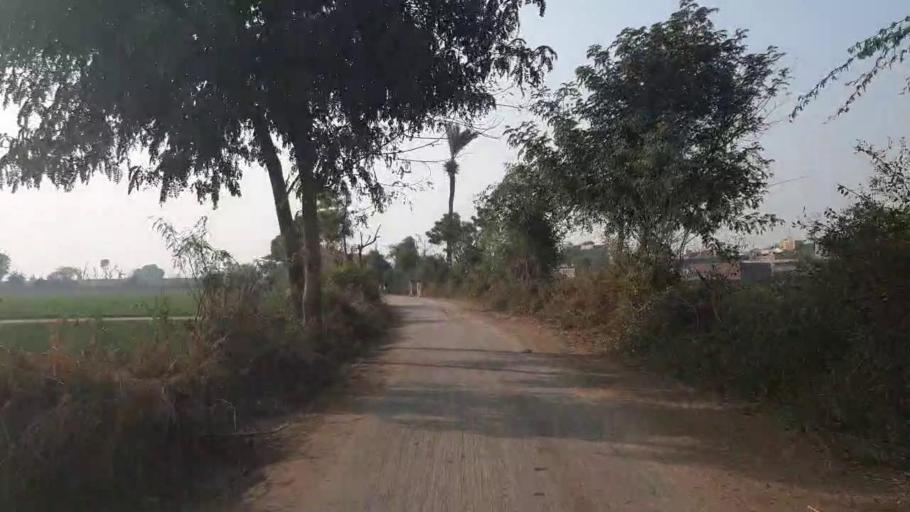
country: PK
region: Sindh
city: Hala
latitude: 25.7869
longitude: 68.3913
